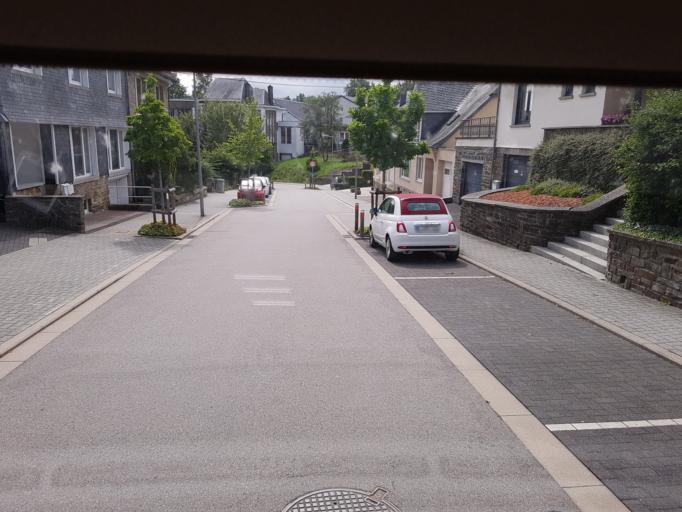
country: BE
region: Wallonia
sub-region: Province de Liege
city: Saint-Vith
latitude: 50.2808
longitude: 6.1285
